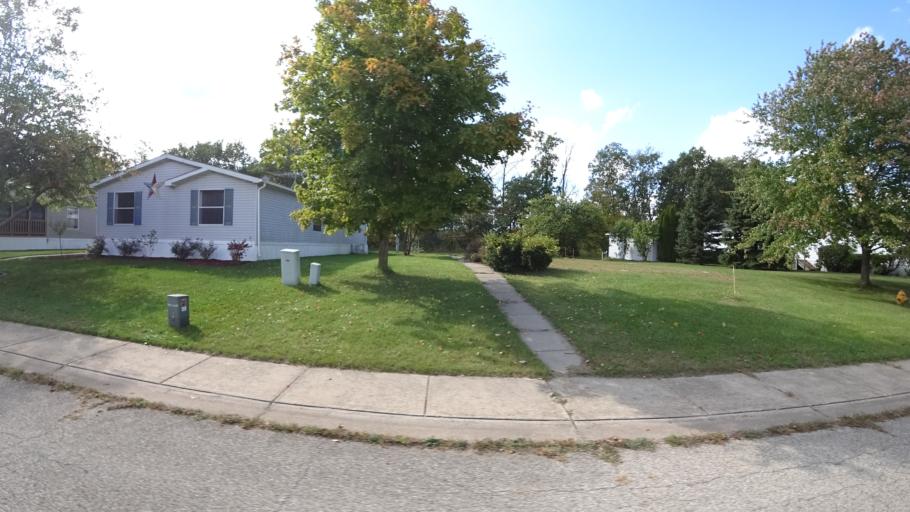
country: US
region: Michigan
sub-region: Saint Joseph County
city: Three Rivers
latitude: 41.9560
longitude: -85.6182
